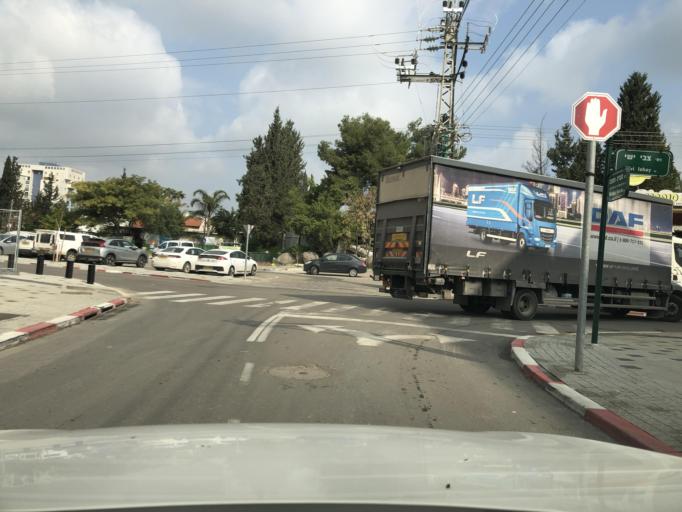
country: IL
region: Central District
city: Yehud
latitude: 32.0324
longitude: 34.8884
